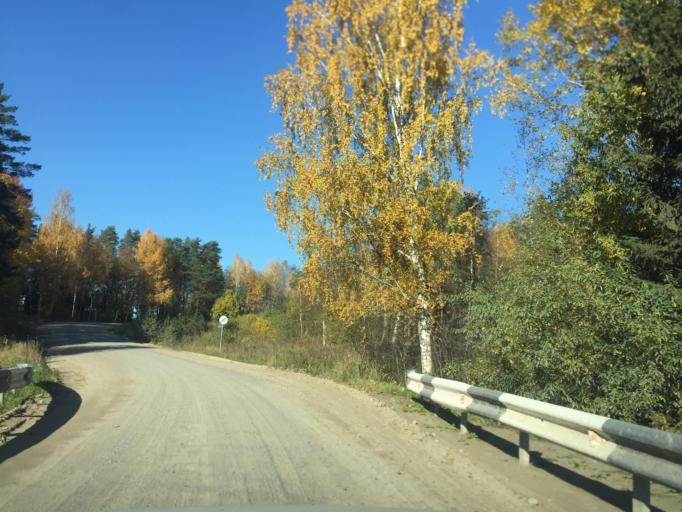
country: RU
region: Leningrad
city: Kuznechnoye
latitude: 61.3239
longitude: 29.9465
